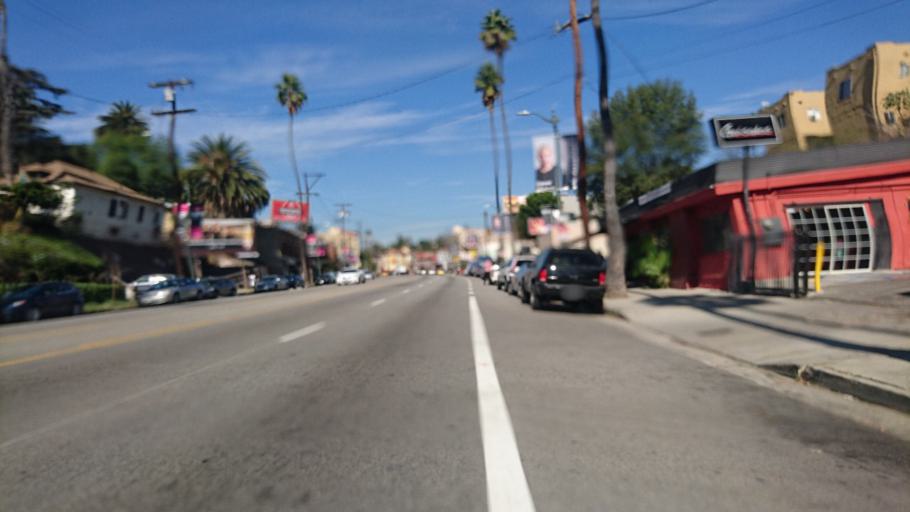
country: US
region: California
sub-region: Los Angeles County
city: Echo Park
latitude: 34.0700
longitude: -118.2504
